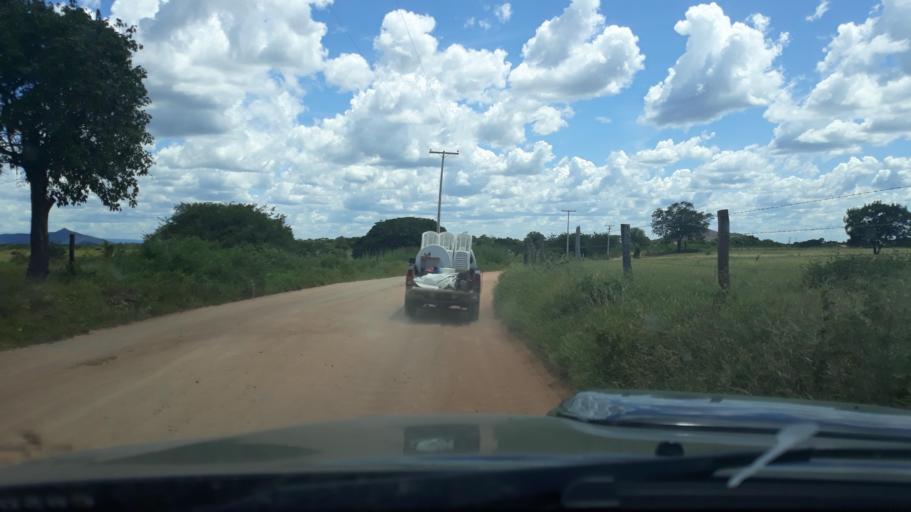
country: BR
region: Bahia
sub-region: Riacho De Santana
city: Riacho de Santana
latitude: -13.9044
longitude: -42.8976
